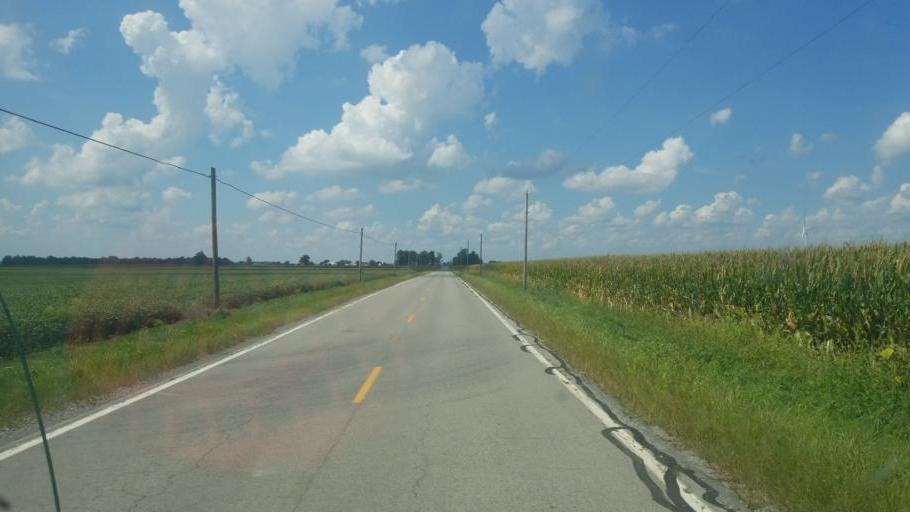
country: US
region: Ohio
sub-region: Hardin County
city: Ada
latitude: 40.7764
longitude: -83.7401
